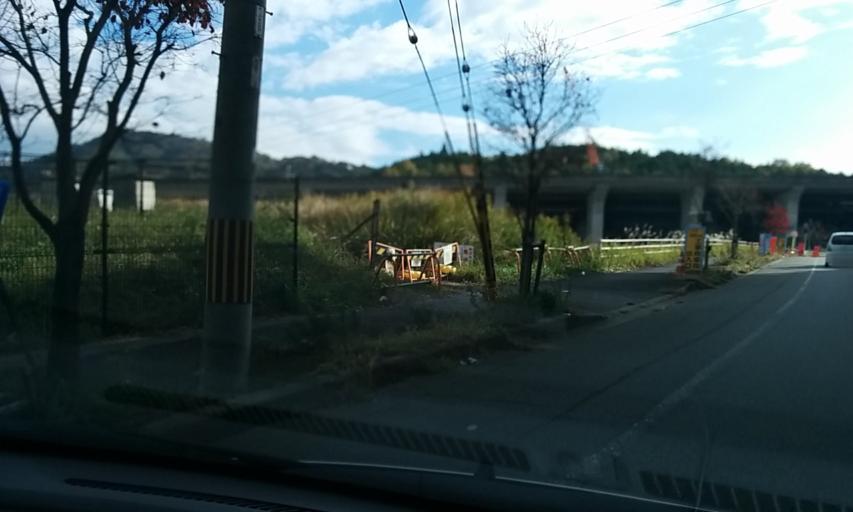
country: JP
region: Kyoto
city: Fukuchiyama
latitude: 35.2953
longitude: 135.1782
